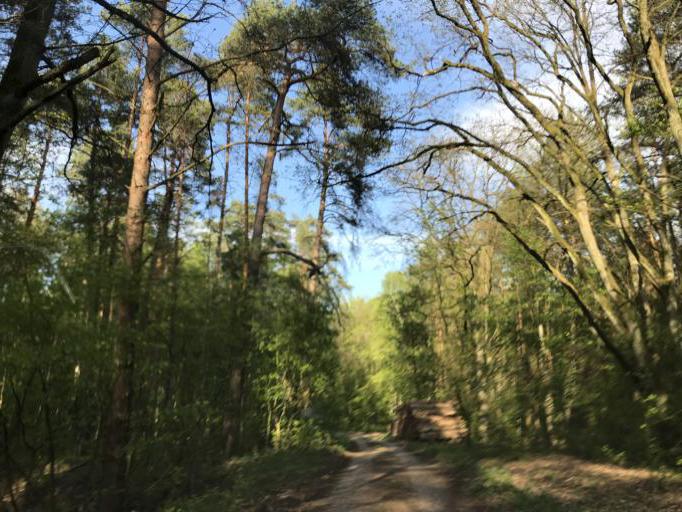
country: DE
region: Brandenburg
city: Joachimsthal
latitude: 52.9632
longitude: 13.7099
